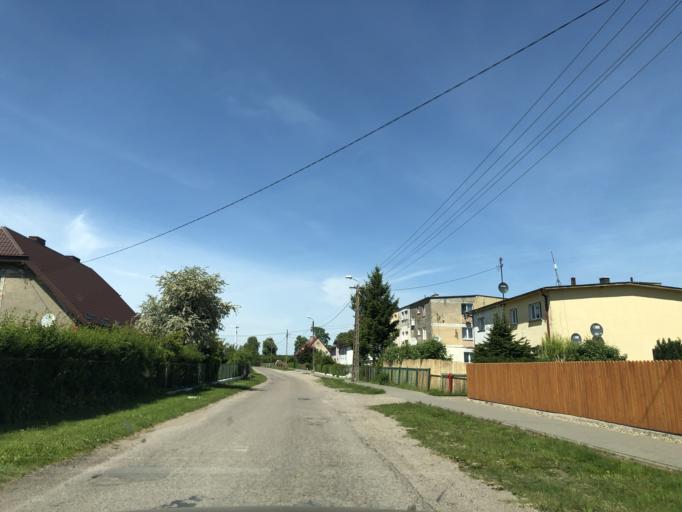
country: PL
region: West Pomeranian Voivodeship
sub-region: Powiat kolobrzeski
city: Goscino
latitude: 54.0485
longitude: 15.7288
